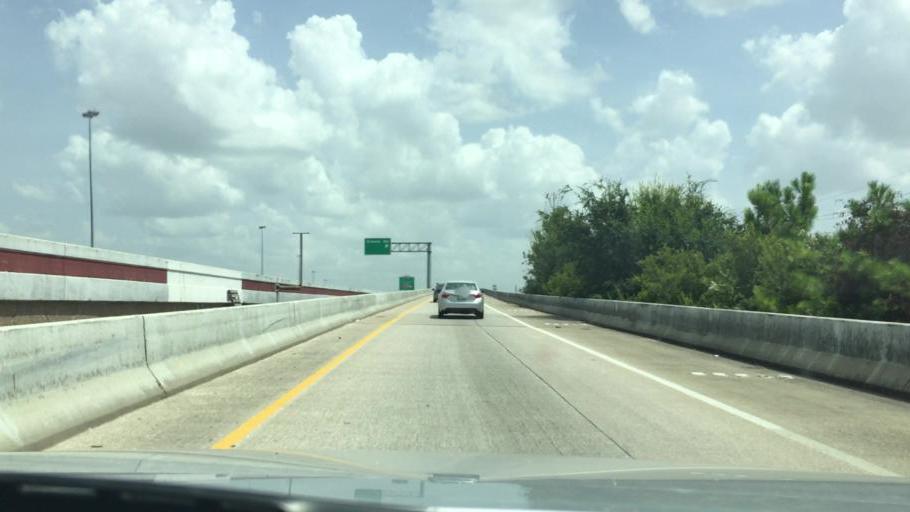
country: US
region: Texas
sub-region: Harris County
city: Hudson
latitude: 29.9576
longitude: -95.5442
